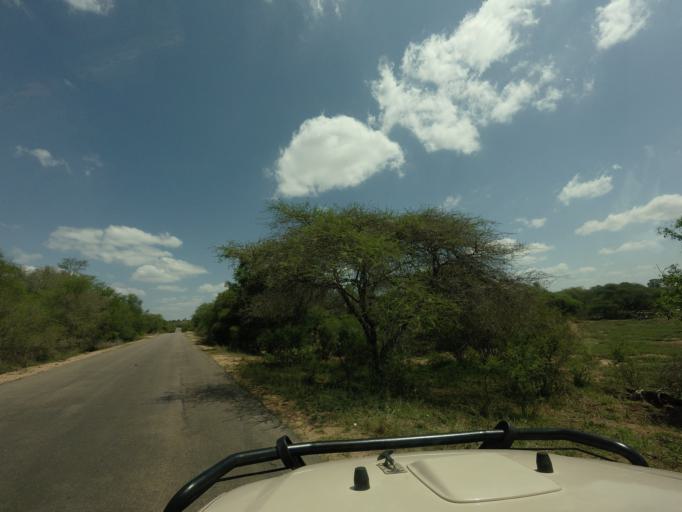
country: ZA
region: Mpumalanga
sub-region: Ehlanzeni District
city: Komatipoort
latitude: -25.0548
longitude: 31.8022
